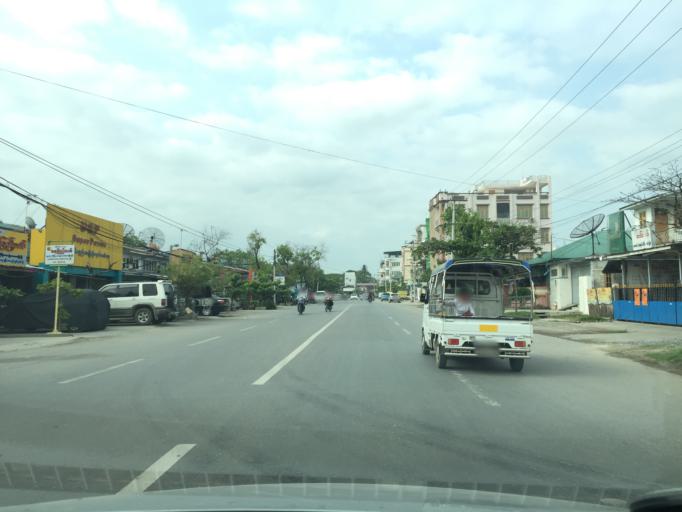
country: MM
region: Mandalay
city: Mandalay
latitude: 21.9705
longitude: 96.1030
